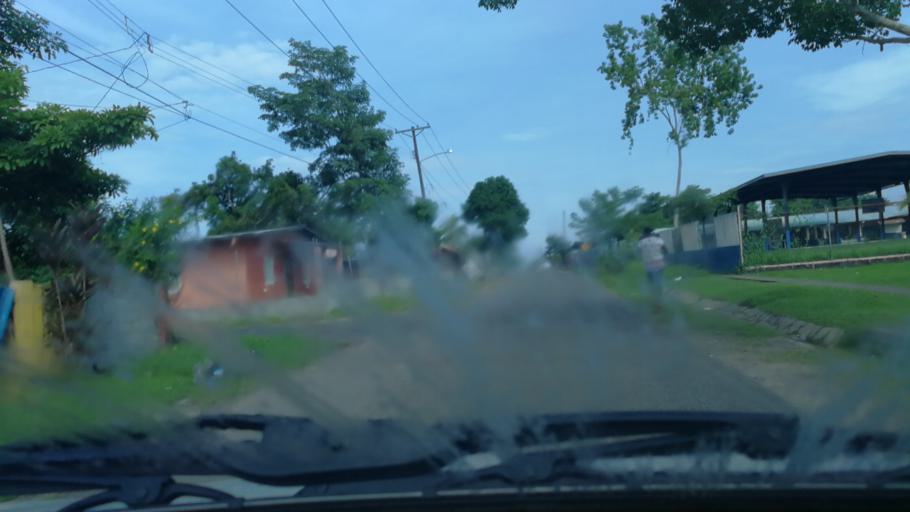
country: PA
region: Panama
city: Pacora
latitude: 9.0850
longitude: -79.2904
